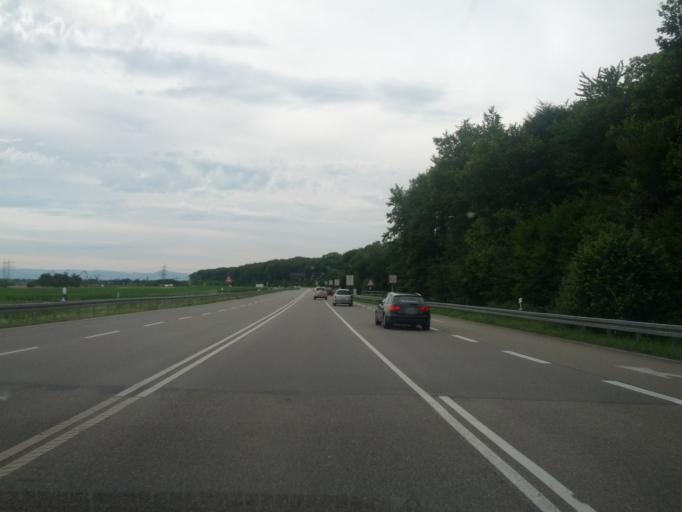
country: DE
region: Baden-Wuerttemberg
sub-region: Freiburg Region
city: Ringsheim
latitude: 48.2538
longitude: 7.7575
